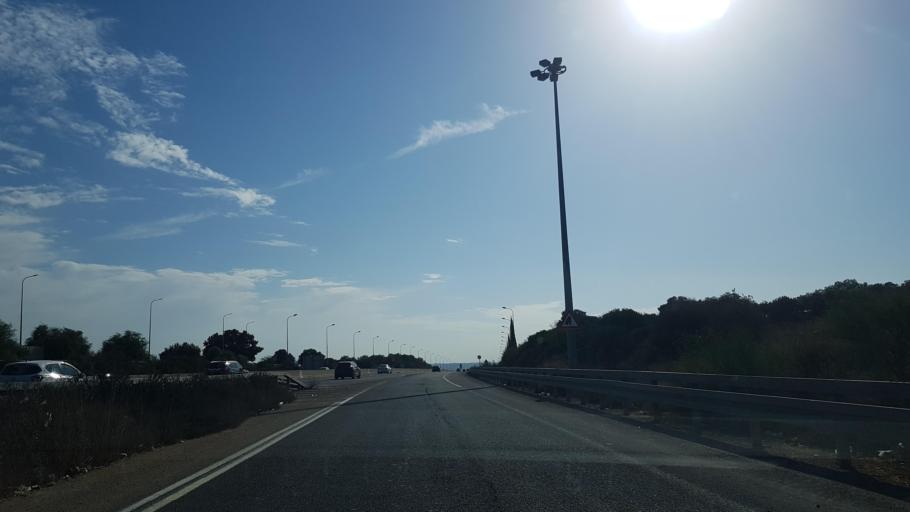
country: IL
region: Northern District
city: Timrat
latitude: 32.7337
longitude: 35.2103
